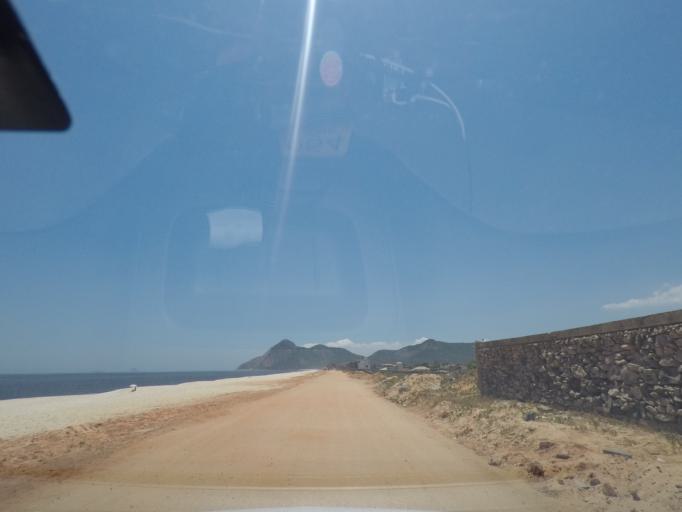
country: BR
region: Rio de Janeiro
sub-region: Niteroi
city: Niteroi
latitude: -22.9694
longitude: -42.9706
